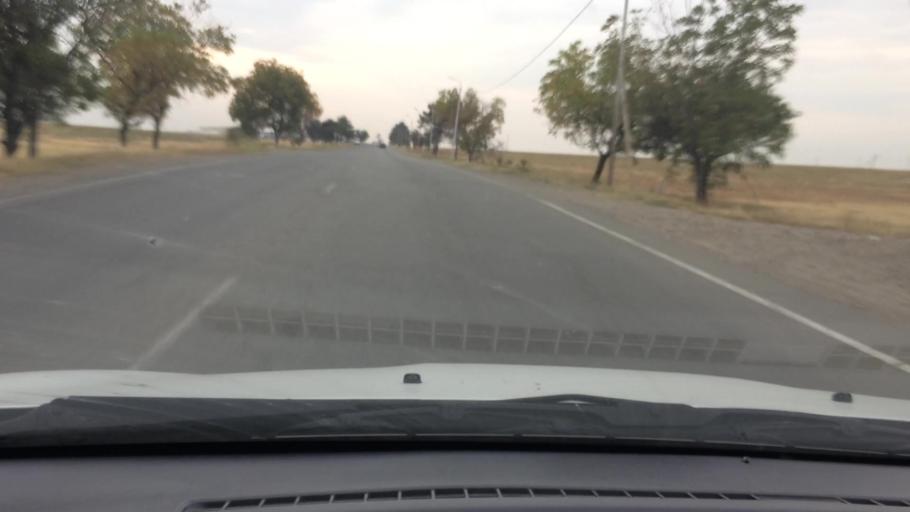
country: GE
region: Kvemo Kartli
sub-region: Marneuli
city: Marneuli
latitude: 41.5170
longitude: 44.7836
